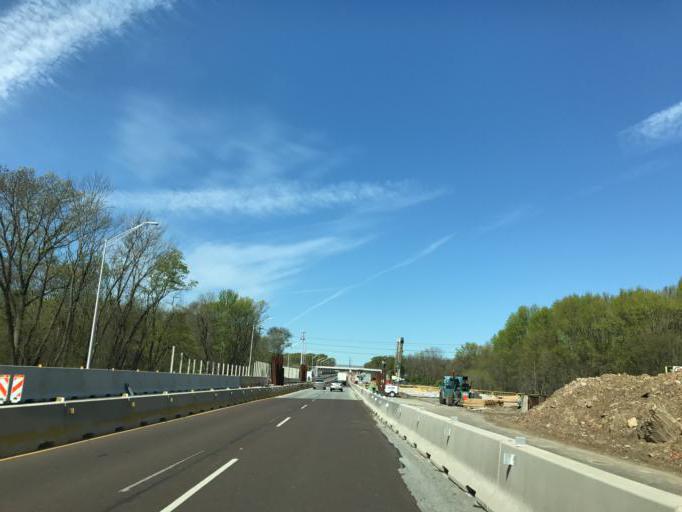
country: US
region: Pennsylvania
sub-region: Bucks County
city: Bristol
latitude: 40.1245
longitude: -74.8595
